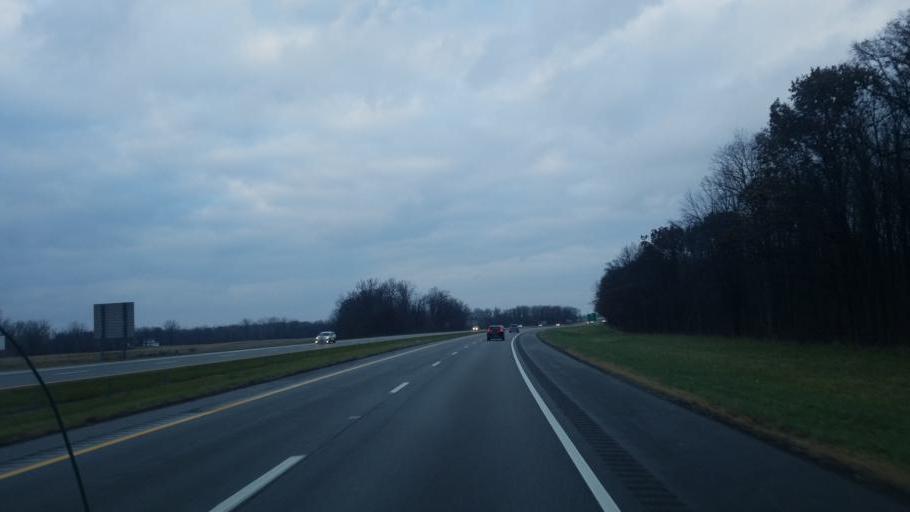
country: US
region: Ohio
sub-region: Auglaize County
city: Wapakoneta
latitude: 40.5739
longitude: -84.1698
